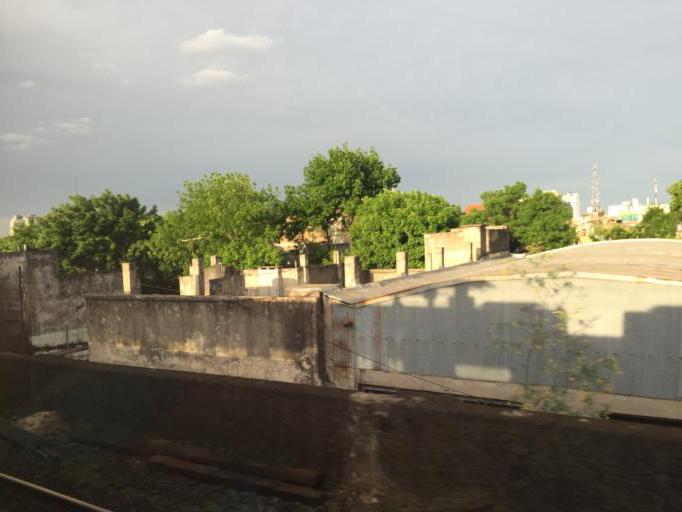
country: AR
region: Buenos Aires
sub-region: Partido de Avellaneda
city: Avellaneda
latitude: -34.6477
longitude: -58.3804
